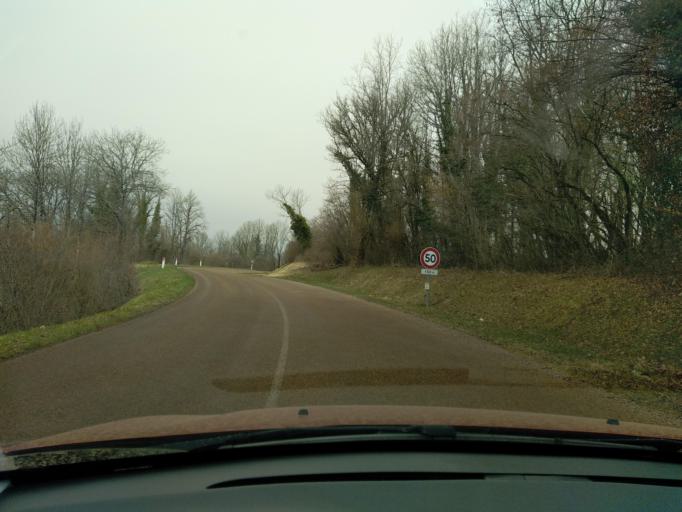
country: FR
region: Franche-Comte
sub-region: Departement du Jura
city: Clairvaux-les-Lacs
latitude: 46.6447
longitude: 5.7564
